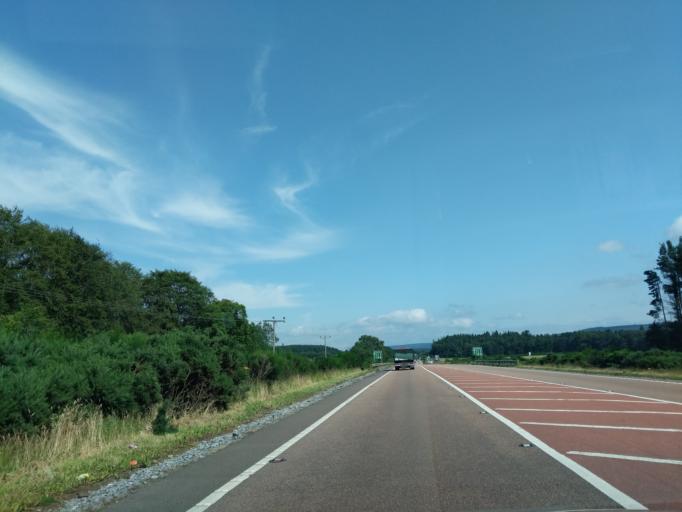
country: GB
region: Scotland
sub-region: Moray
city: Fochabers
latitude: 57.6231
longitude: -3.1291
